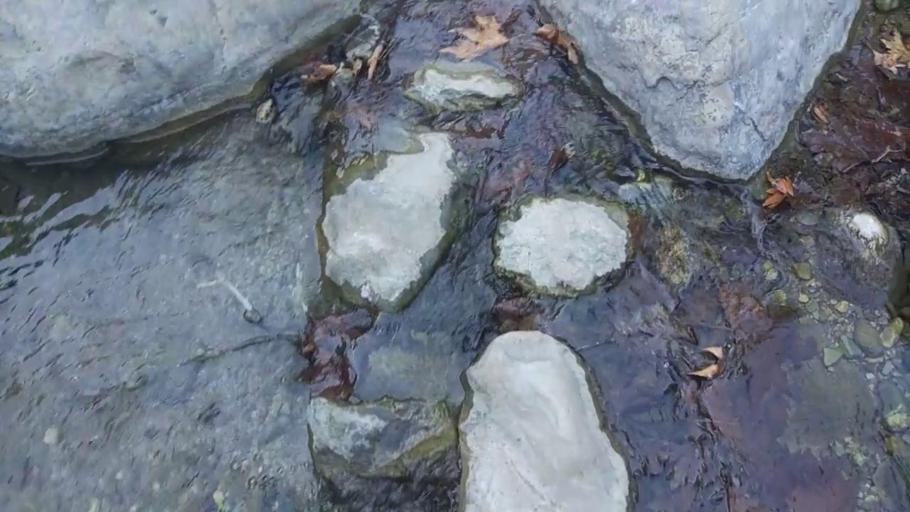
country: TR
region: Antalya
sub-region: Kemer
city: Goeynuek
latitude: 36.6781
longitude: 30.4882
